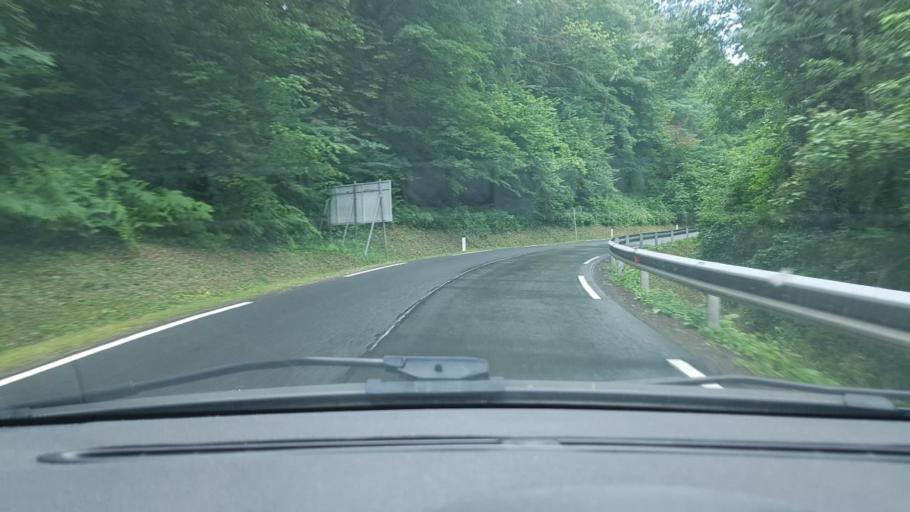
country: AT
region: Styria
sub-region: Politischer Bezirk Suedoststeiermark
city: Mureck
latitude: 46.6964
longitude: 15.7855
